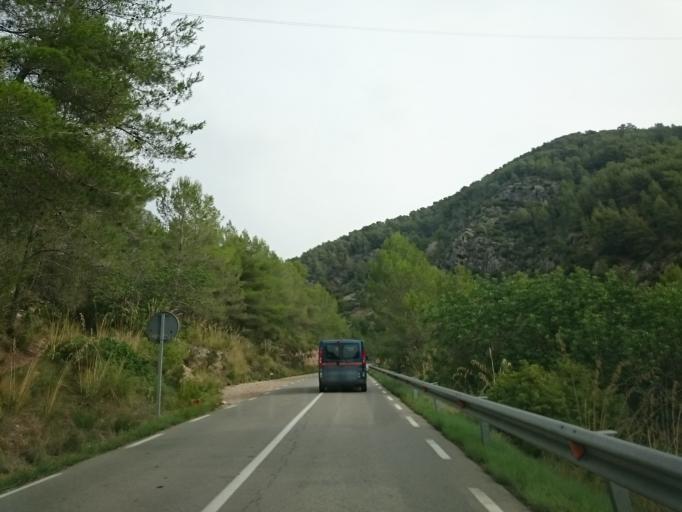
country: ES
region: Catalonia
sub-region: Provincia de Barcelona
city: Sant Pere de Ribes
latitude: 41.2812
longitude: 1.7830
